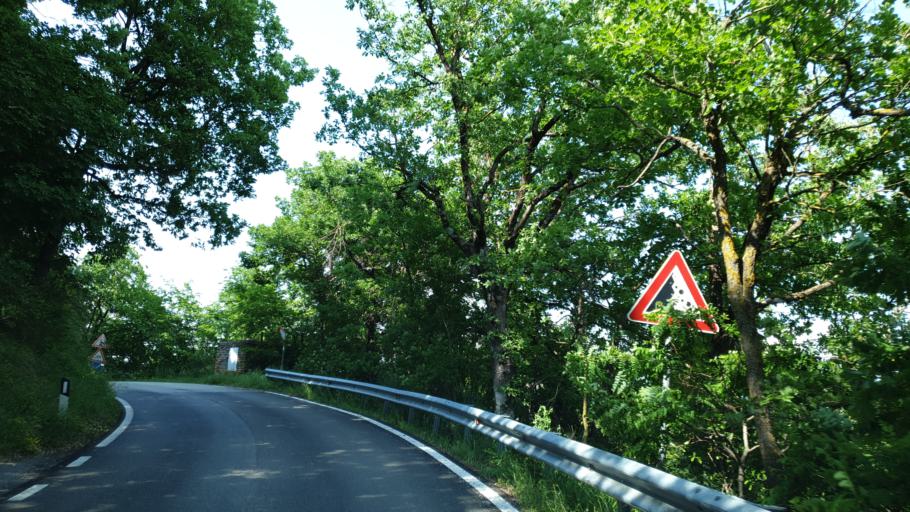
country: IT
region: Emilia-Romagna
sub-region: Forli-Cesena
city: Sarsina
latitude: 43.9085
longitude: 12.1780
